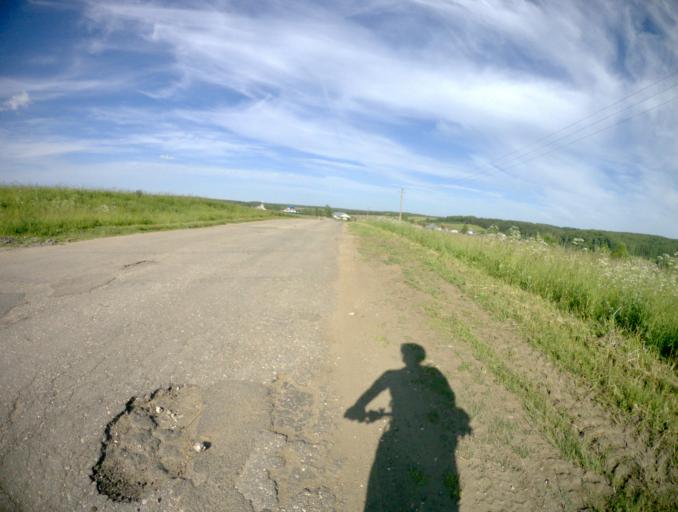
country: RU
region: Vladimir
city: Vorsha
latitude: 56.1692
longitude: 40.1520
